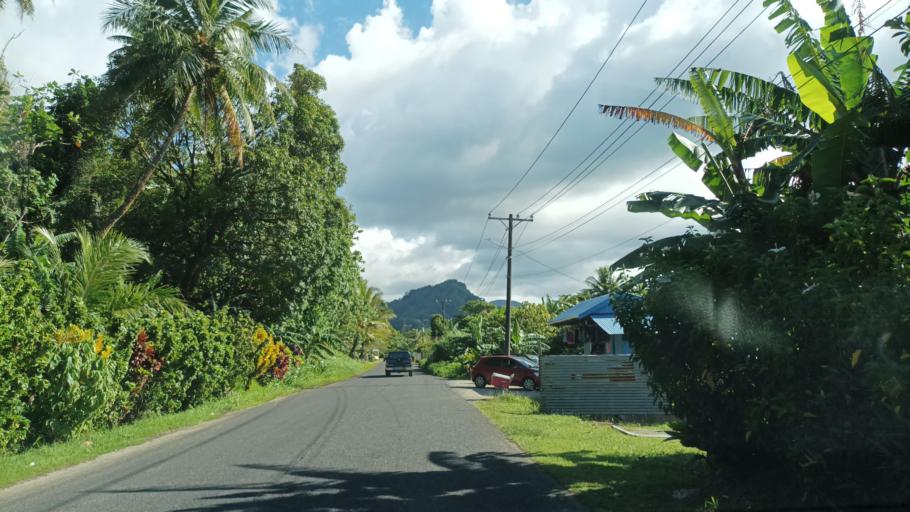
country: FM
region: Pohnpei
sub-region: Kolonia Municipality
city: Kolonia
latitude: 6.9656
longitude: 158.2507
